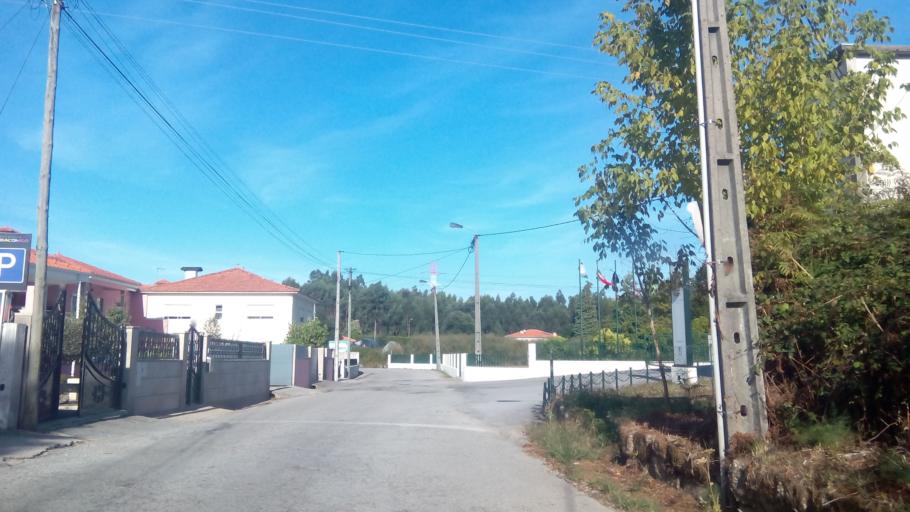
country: PT
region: Porto
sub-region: Paredes
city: Baltar
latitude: 41.1768
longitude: -8.3831
